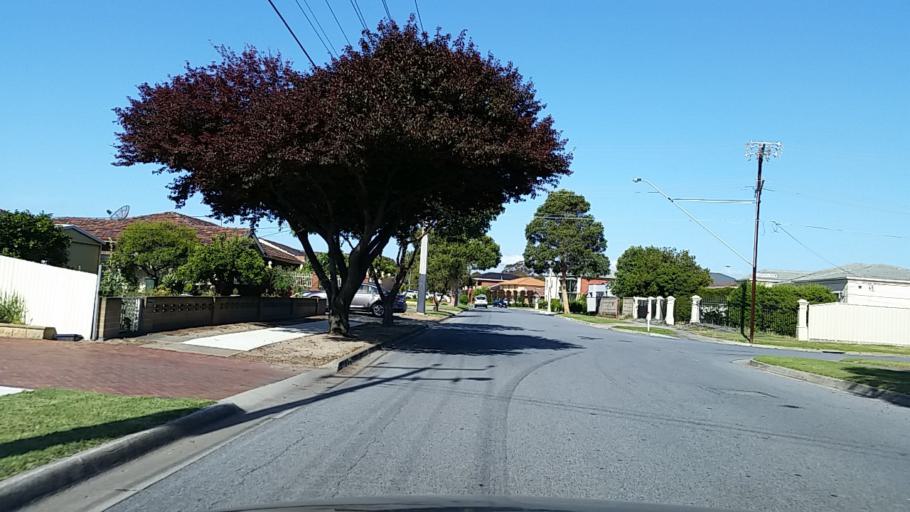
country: AU
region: South Australia
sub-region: Charles Sturt
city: Henley Beach
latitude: -34.9203
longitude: 138.5086
